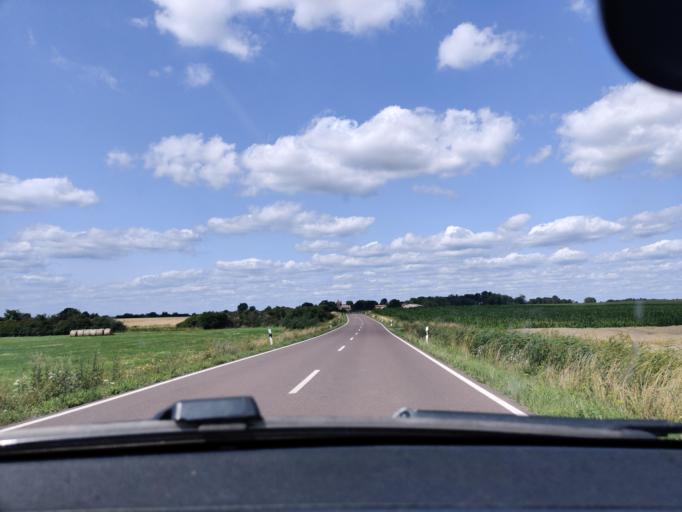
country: DE
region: Saxony-Anhalt
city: Loburg
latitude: 52.0797
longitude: 12.0478
